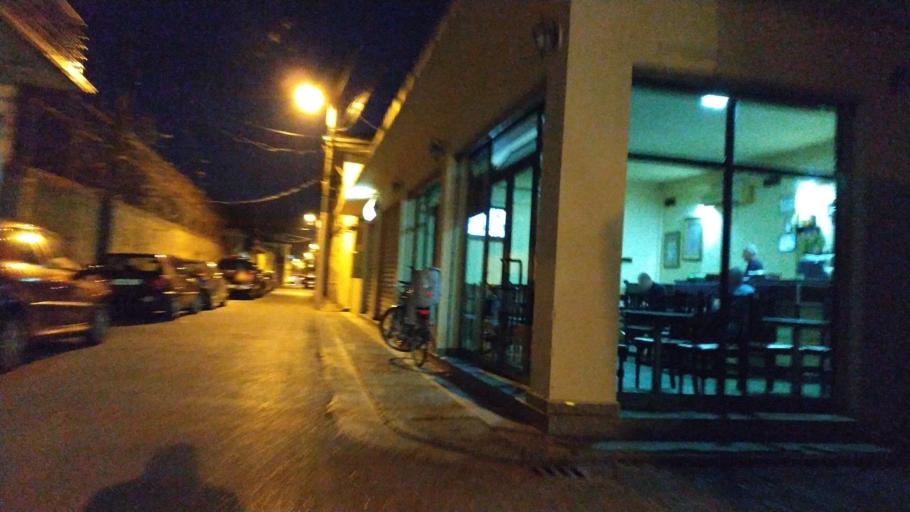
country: AL
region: Shkoder
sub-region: Rrethi i Shkodres
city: Shkoder
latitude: 42.0670
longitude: 19.5079
